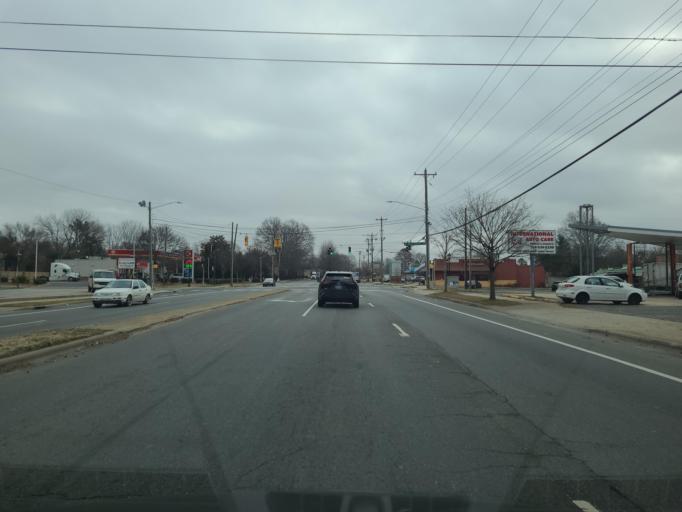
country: US
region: North Carolina
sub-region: Mecklenburg County
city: Charlotte
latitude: 35.2123
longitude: -80.7635
